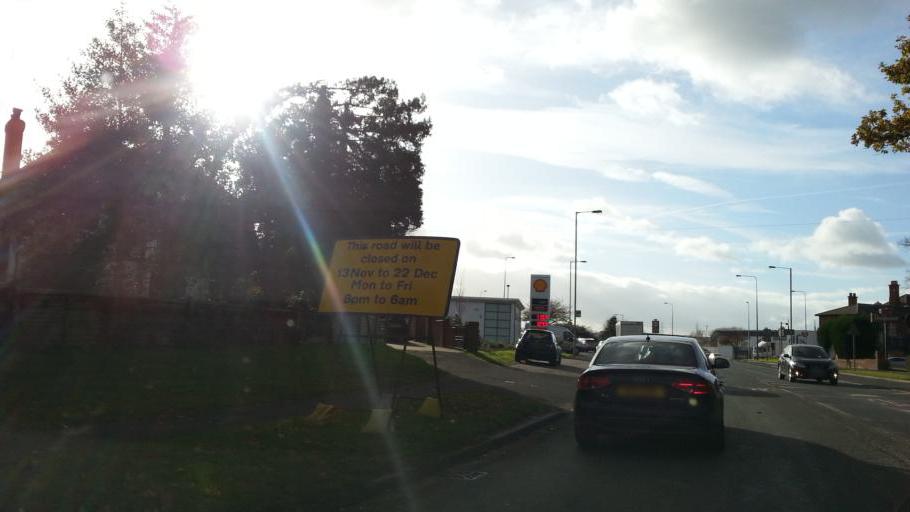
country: GB
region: England
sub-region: Staffordshire
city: Cannock
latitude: 52.6803
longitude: -2.0475
